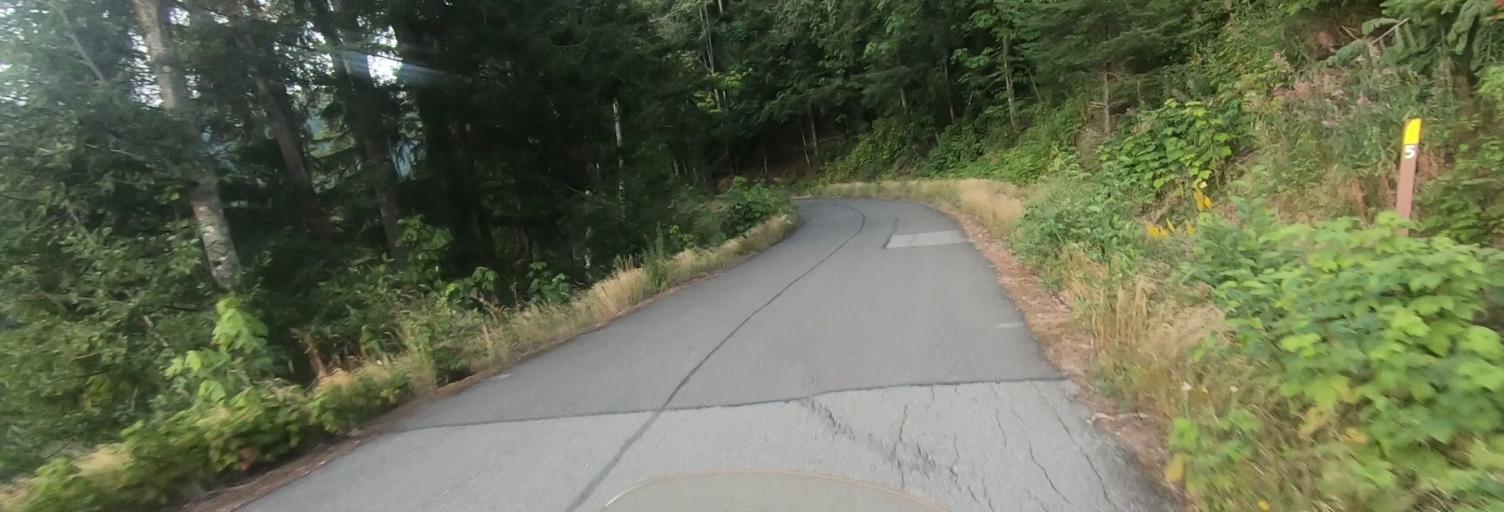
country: US
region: Washington
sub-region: Whatcom County
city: Peaceful Valley
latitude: 48.9252
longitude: -121.9565
